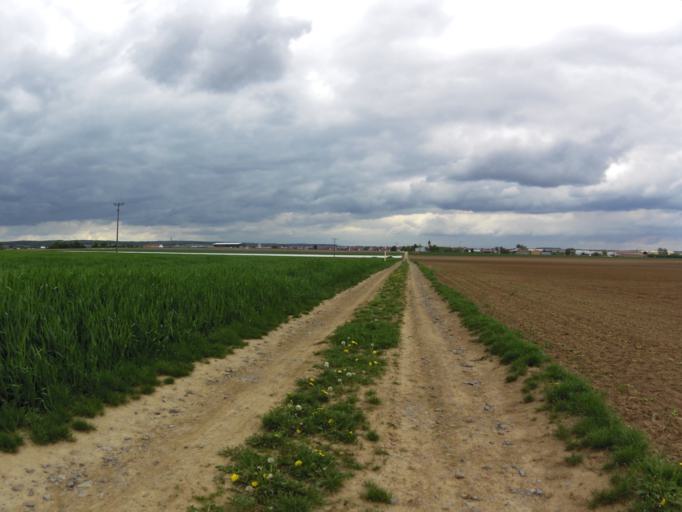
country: DE
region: Bavaria
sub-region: Regierungsbezirk Unterfranken
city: Unterpleichfeld
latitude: 49.8570
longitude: 10.0493
